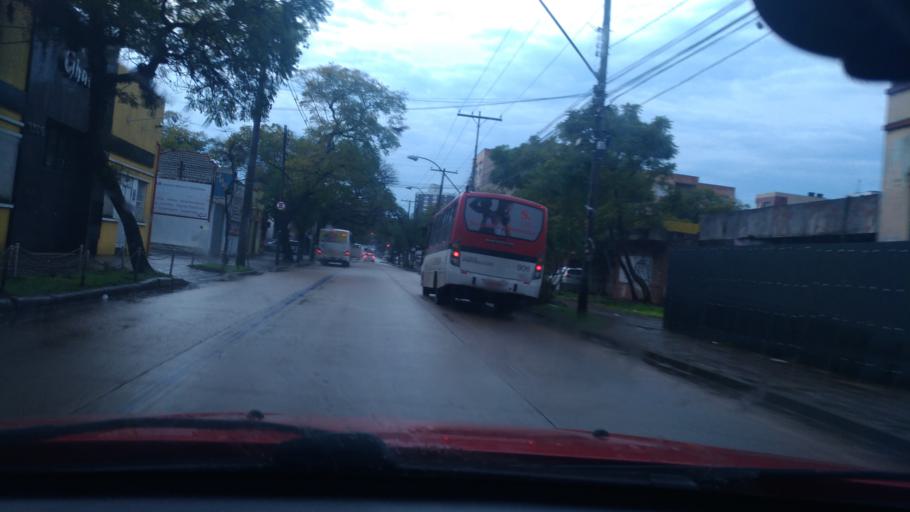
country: BR
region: Rio Grande do Sul
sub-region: Porto Alegre
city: Porto Alegre
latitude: -30.0068
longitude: -51.1956
